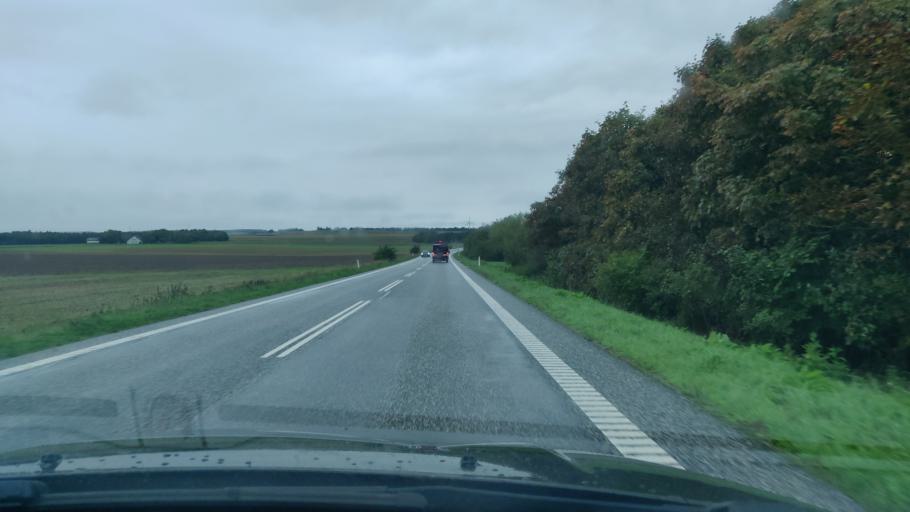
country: DK
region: North Denmark
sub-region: Thisted Kommune
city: Thisted
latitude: 56.9775
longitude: 8.7561
